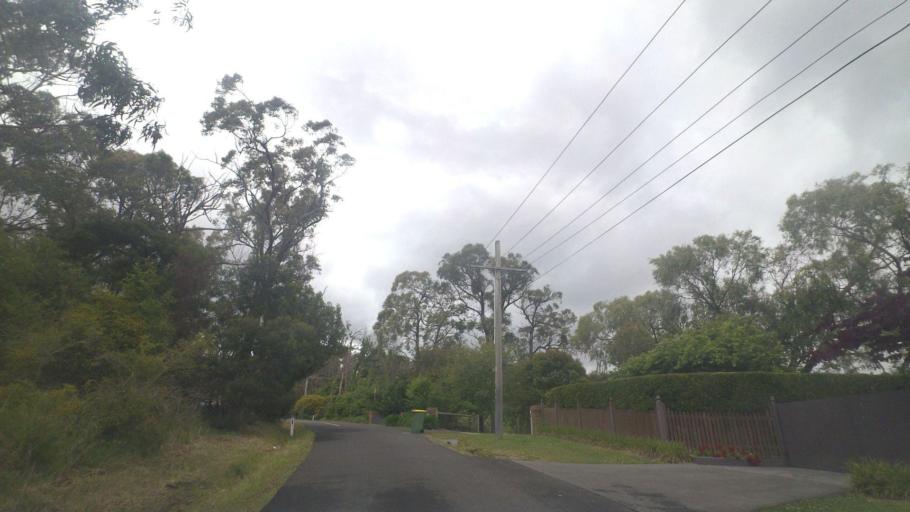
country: AU
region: Victoria
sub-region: Yarra Ranges
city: Mount Evelyn
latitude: -37.7796
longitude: 145.3718
